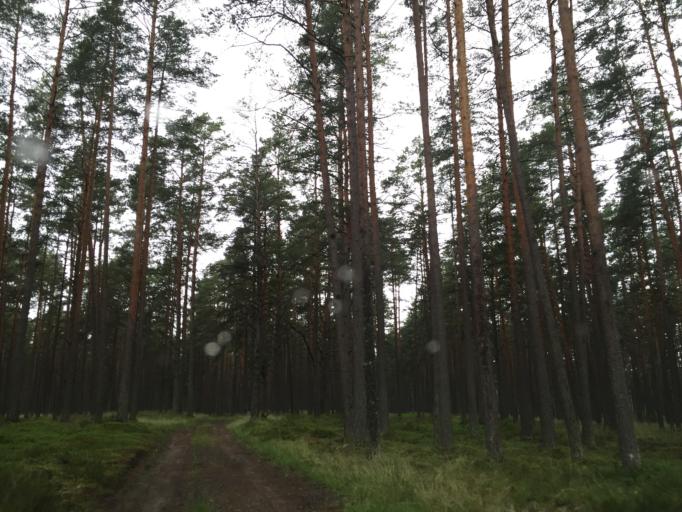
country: LV
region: Riga
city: Jaunciems
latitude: 57.0515
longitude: 24.2162
